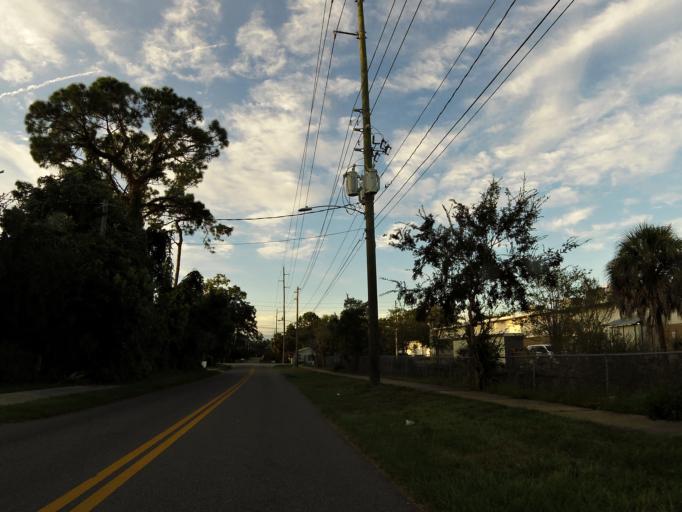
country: US
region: Florida
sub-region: Duval County
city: Jacksonville
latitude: 30.2876
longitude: -81.7219
